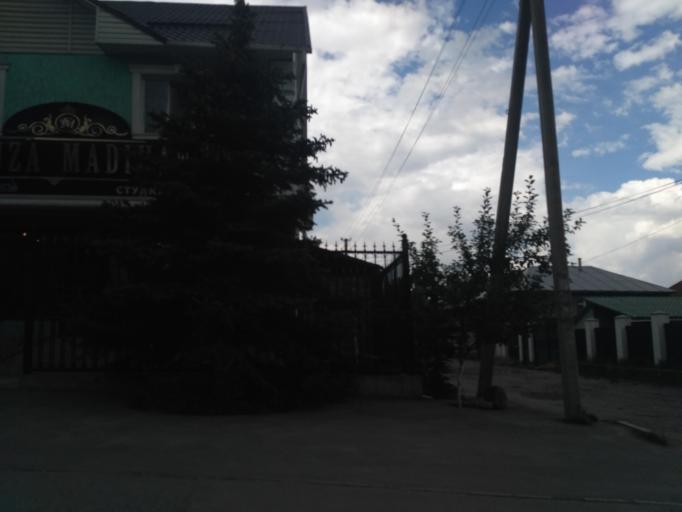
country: KZ
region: Almaty Oblysy
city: Burunday
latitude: 43.2060
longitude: 76.6369
